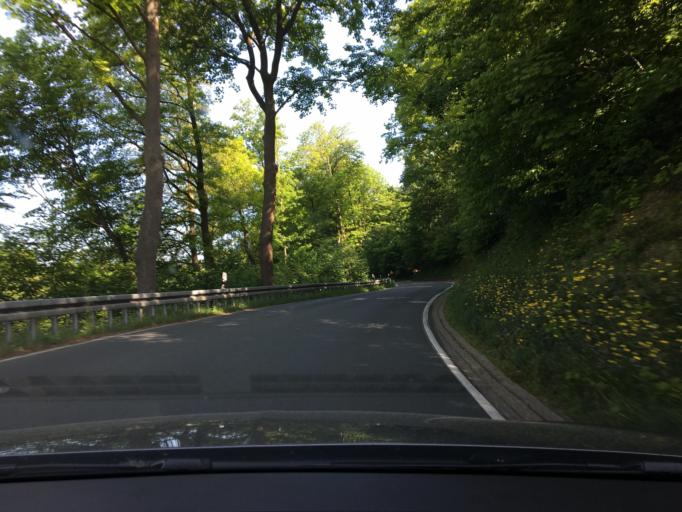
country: DE
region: North Rhine-Westphalia
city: Wickede
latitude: 51.4942
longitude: 7.8510
